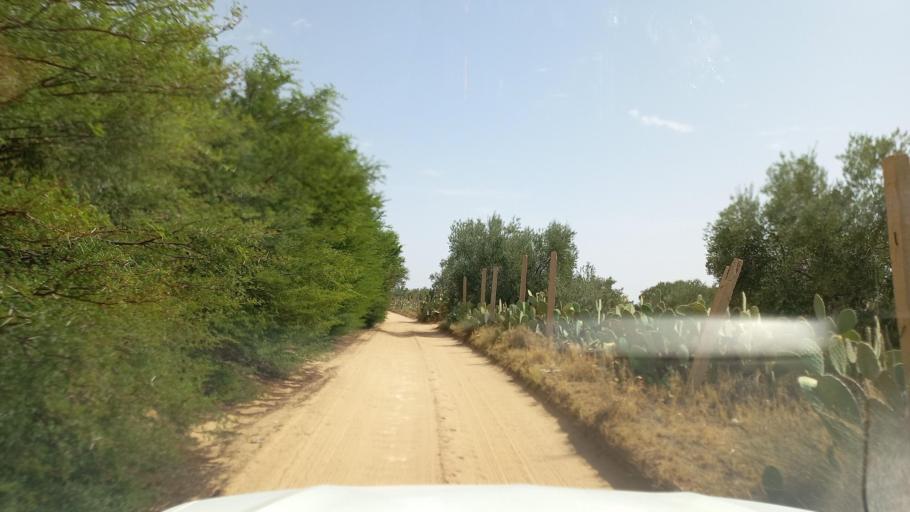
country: TN
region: Al Qasrayn
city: Kasserine
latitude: 35.2562
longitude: 9.0545
